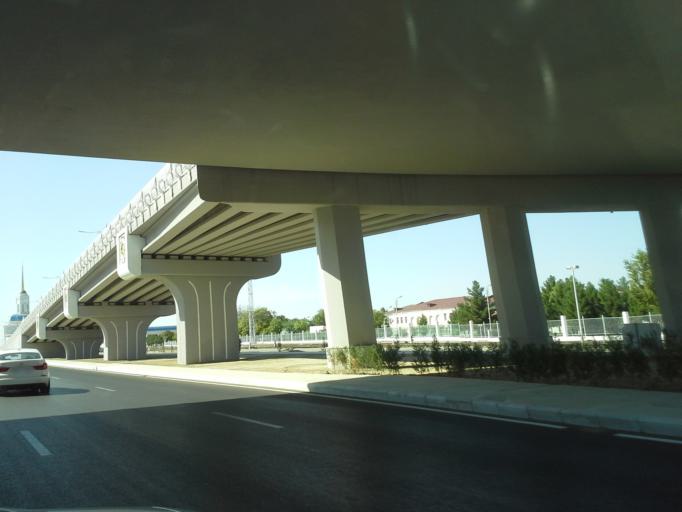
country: TM
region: Ahal
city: Ashgabat
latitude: 37.9405
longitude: 58.4005
